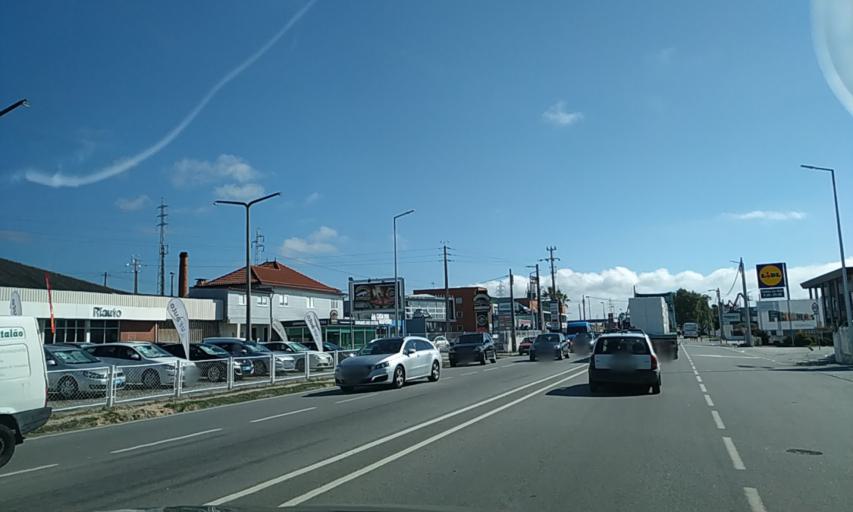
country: PT
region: Aveiro
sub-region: Aveiro
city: Aveiro
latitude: 40.6635
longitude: -8.6117
